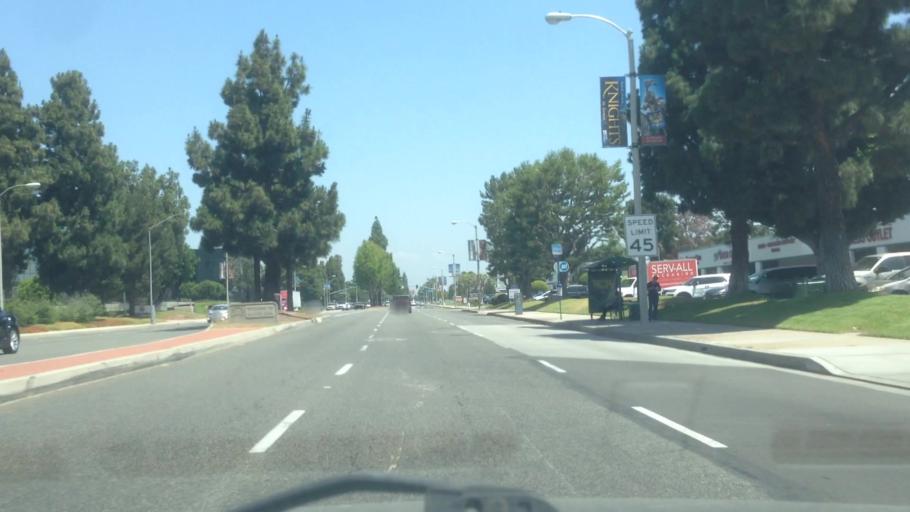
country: US
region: California
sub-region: Orange County
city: Fountain Valley
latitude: 33.7026
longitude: -117.9195
